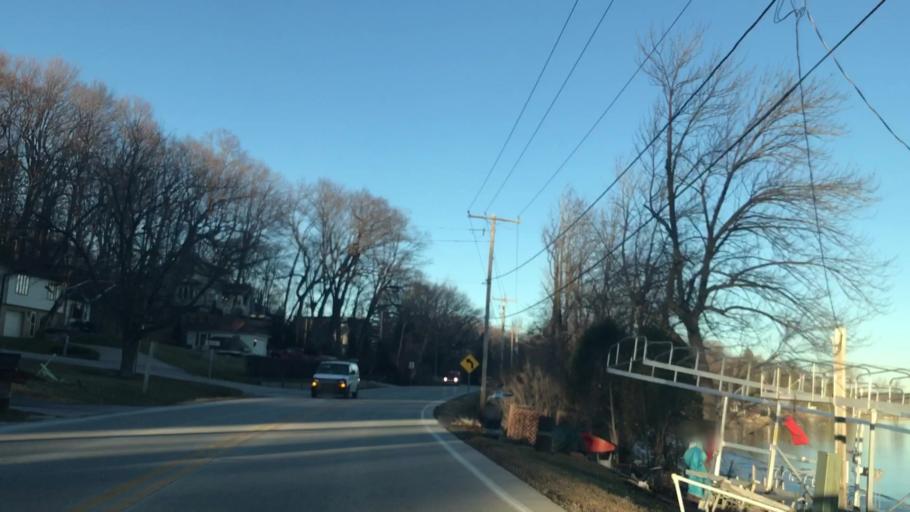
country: US
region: Wisconsin
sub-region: Washington County
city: Slinger
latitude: 43.3716
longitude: -88.2771
